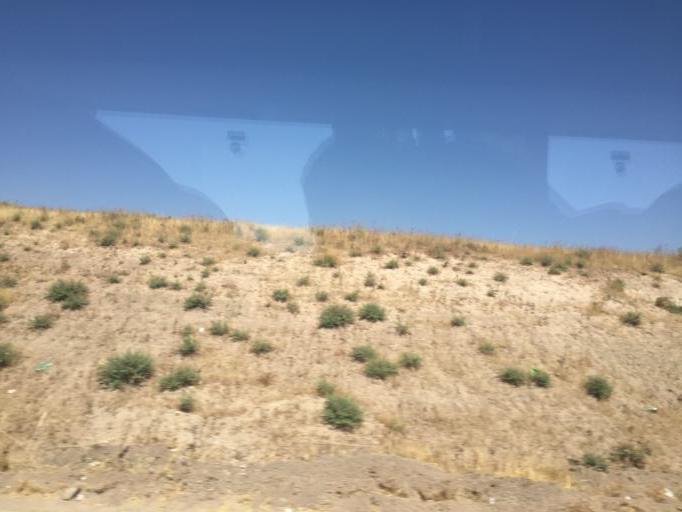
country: TR
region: Diyarbakir
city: Salat
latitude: 37.8596
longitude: 40.8669
